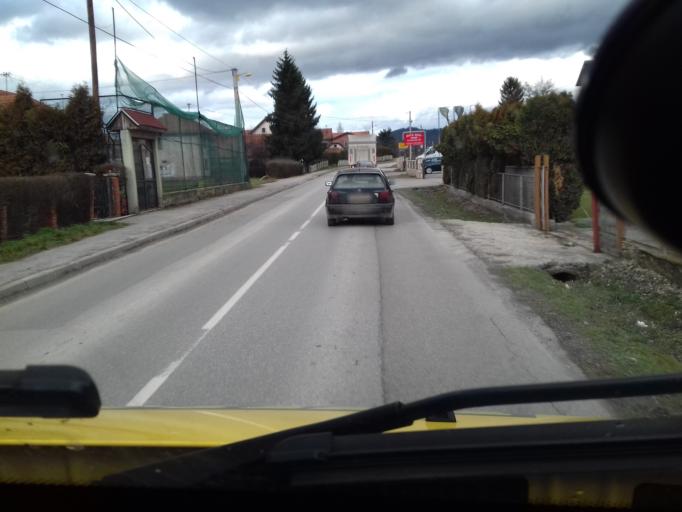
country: BA
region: Federation of Bosnia and Herzegovina
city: Gornje Mostre
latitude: 44.0129
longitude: 18.1420
